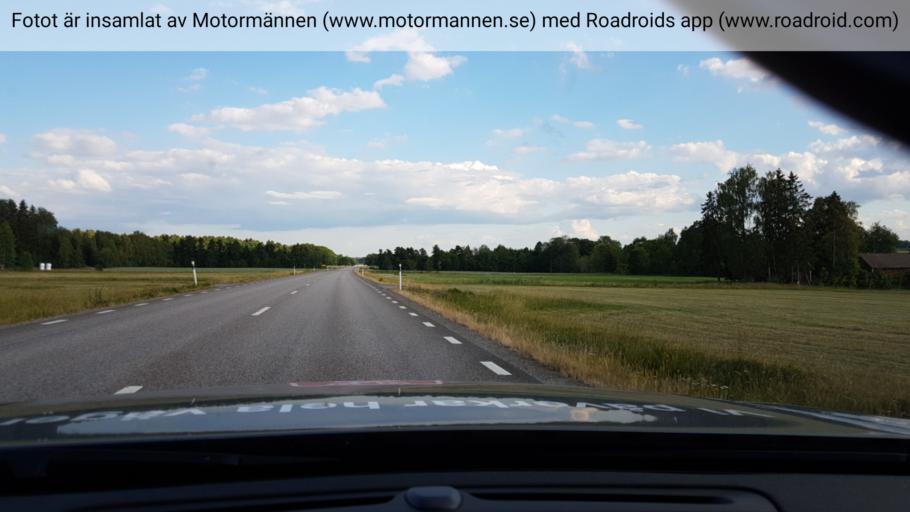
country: SE
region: Uppsala
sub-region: Heby Kommun
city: Heby
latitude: 59.9051
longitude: 16.8956
